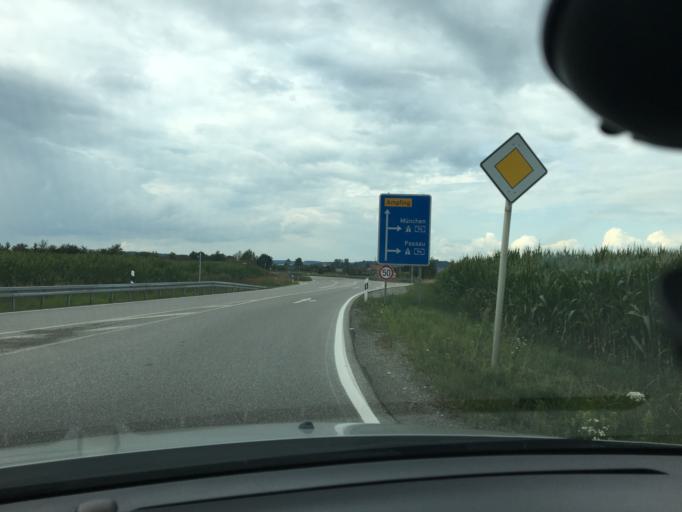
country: DE
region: Bavaria
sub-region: Upper Bavaria
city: Neufahrn
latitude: 48.2500
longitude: 12.4384
